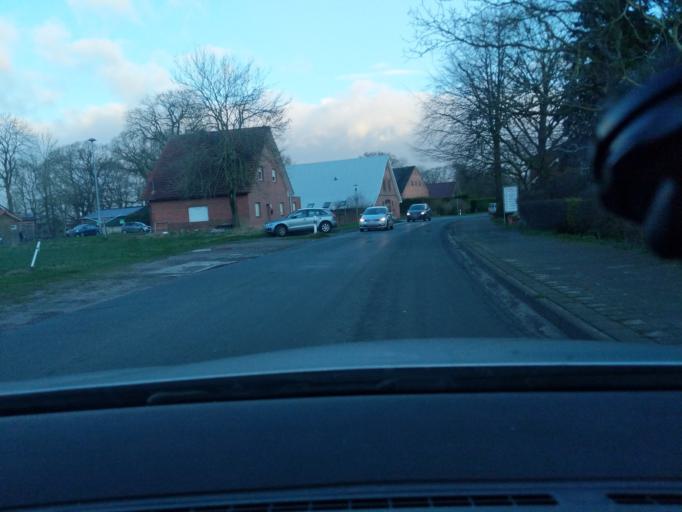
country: DE
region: Lower Saxony
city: Drangstedt
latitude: 53.6369
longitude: 8.7856
